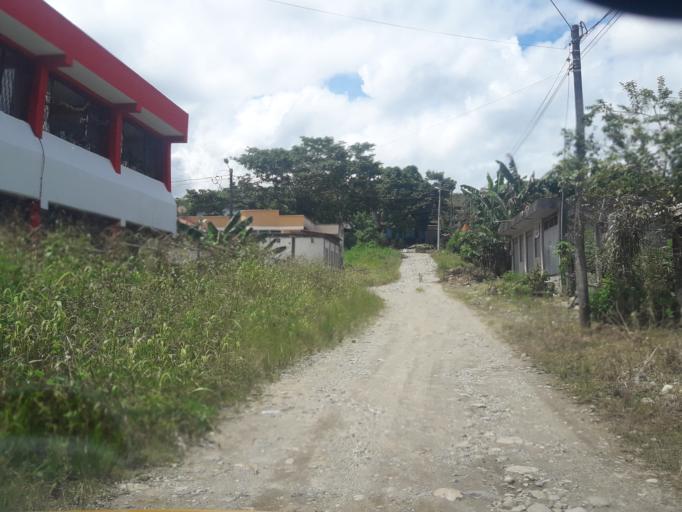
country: EC
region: Napo
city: Tena
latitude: -1.0090
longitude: -77.8118
